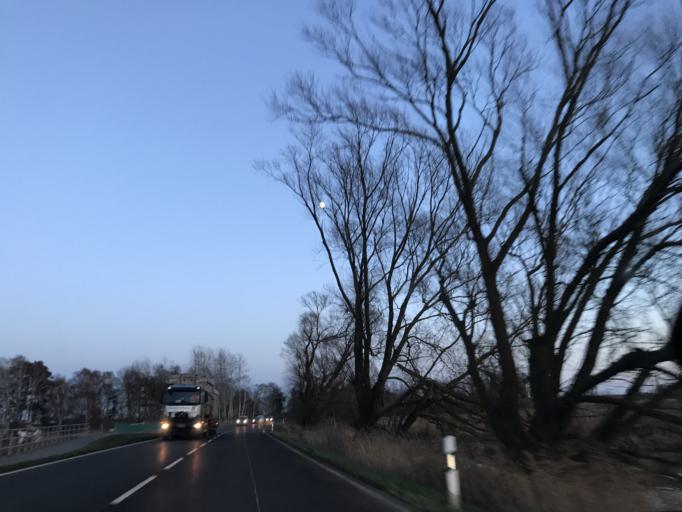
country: DE
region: Brandenburg
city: Premnitz
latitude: 52.5118
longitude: 12.4293
